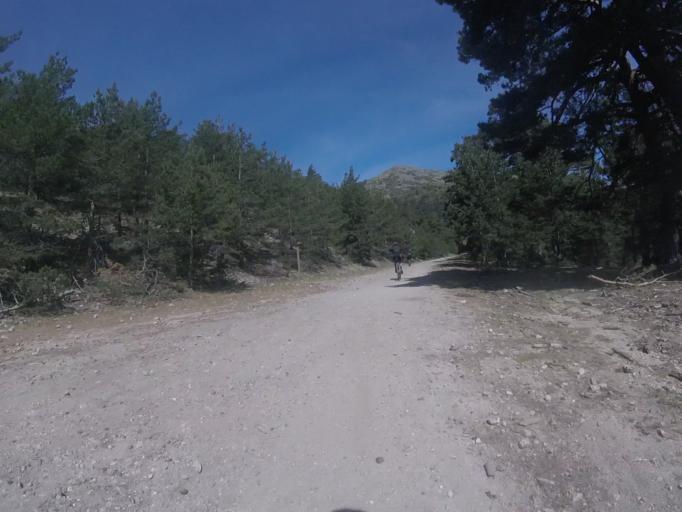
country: ES
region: Madrid
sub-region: Provincia de Madrid
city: Cercedilla
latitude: 40.7928
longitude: -4.0602
